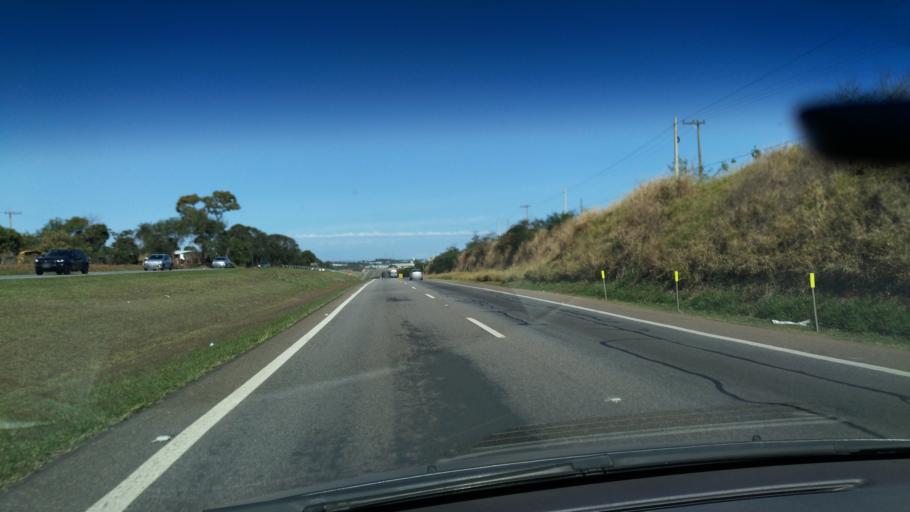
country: BR
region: Sao Paulo
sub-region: Jaguariuna
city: Jaguariuna
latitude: -22.6465
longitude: -47.0058
